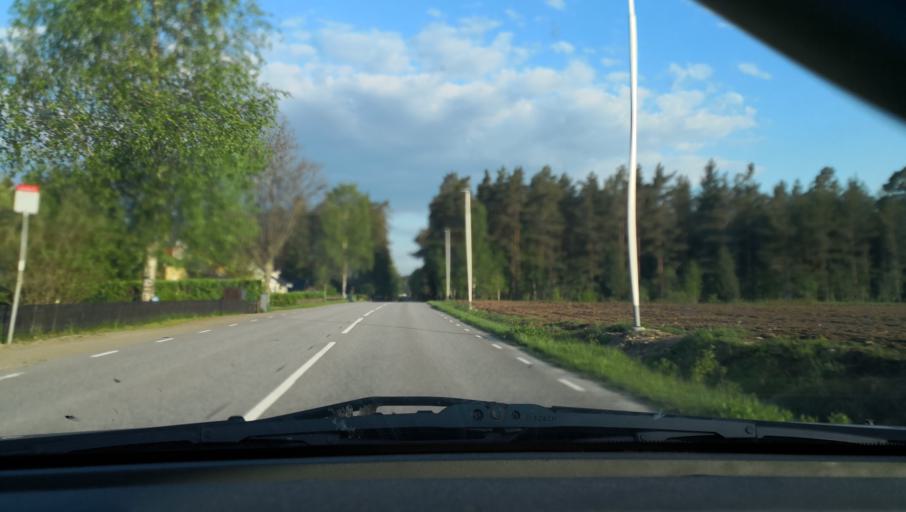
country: SE
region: Joenkoeping
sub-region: Vetlanda Kommun
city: Landsbro
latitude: 57.3753
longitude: 14.8804
